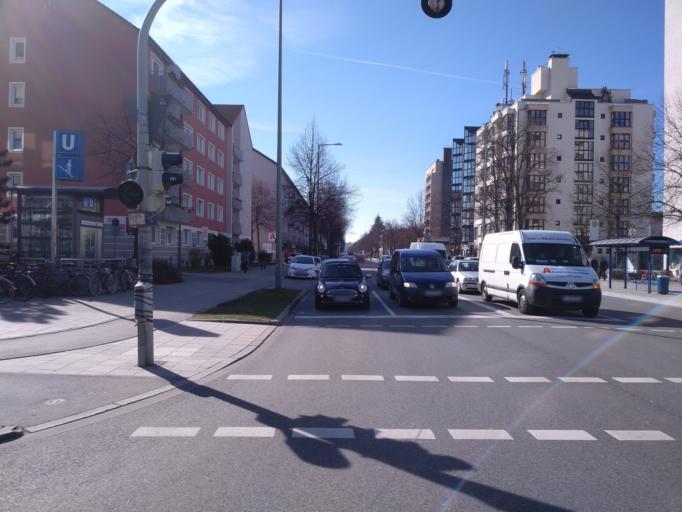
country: DE
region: Bavaria
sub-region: Upper Bavaria
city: Munich
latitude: 48.1874
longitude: 11.5729
